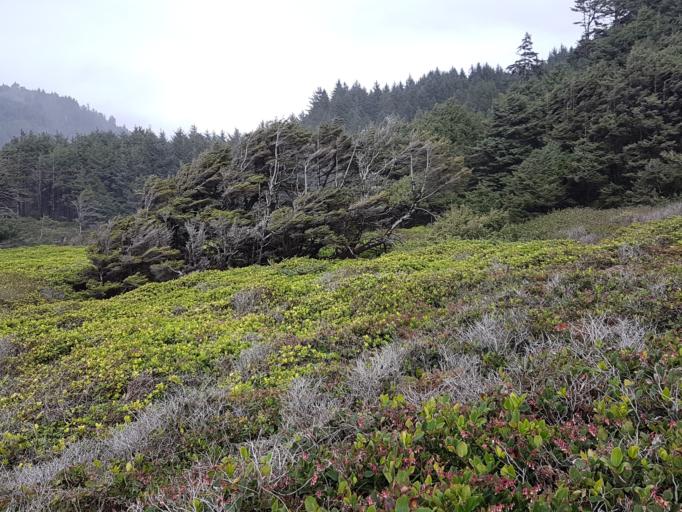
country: US
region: Oregon
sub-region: Lincoln County
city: Waldport
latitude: 44.2791
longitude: -124.1117
